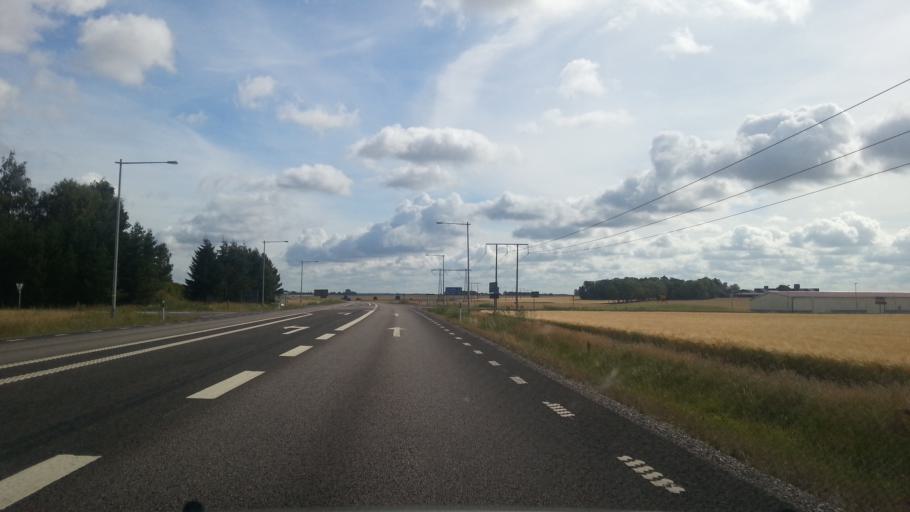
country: SE
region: Vaestra Goetaland
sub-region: Lidkopings Kommun
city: Lidkoping
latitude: 58.4633
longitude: 13.0386
